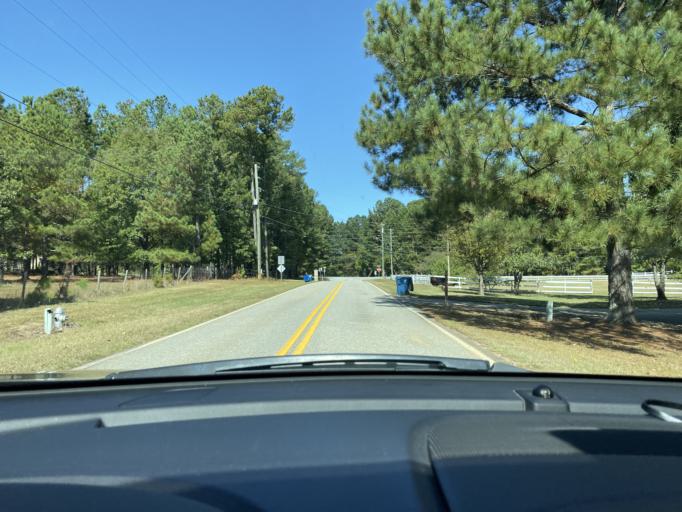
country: US
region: Georgia
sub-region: Gwinnett County
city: Grayson
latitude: 33.8949
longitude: -83.9054
